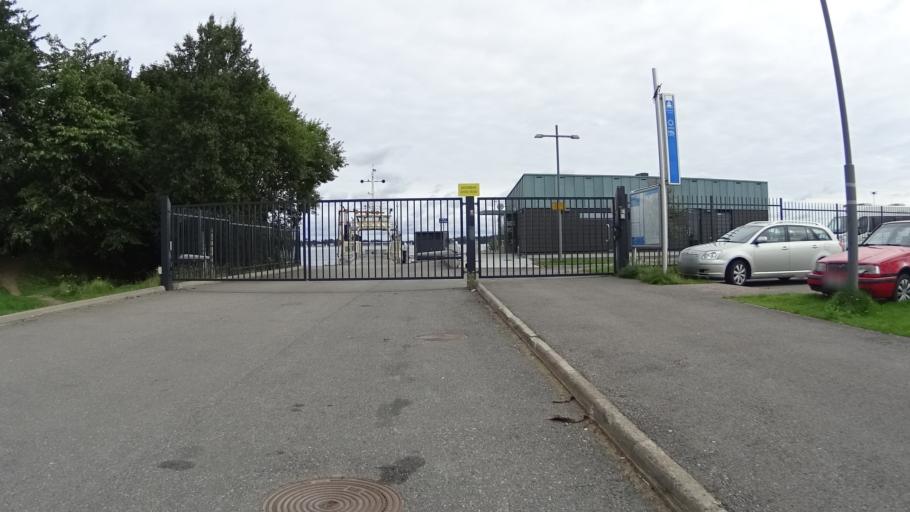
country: FI
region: Uusimaa
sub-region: Helsinki
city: Helsinki
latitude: 60.1669
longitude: 24.9790
